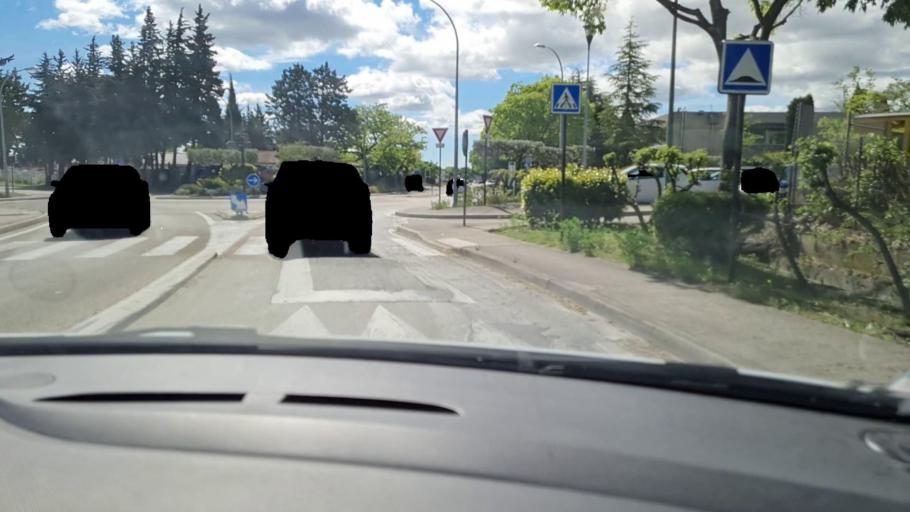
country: FR
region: Languedoc-Roussillon
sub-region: Departement du Gard
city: Milhaud
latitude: 43.8133
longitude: 4.3164
